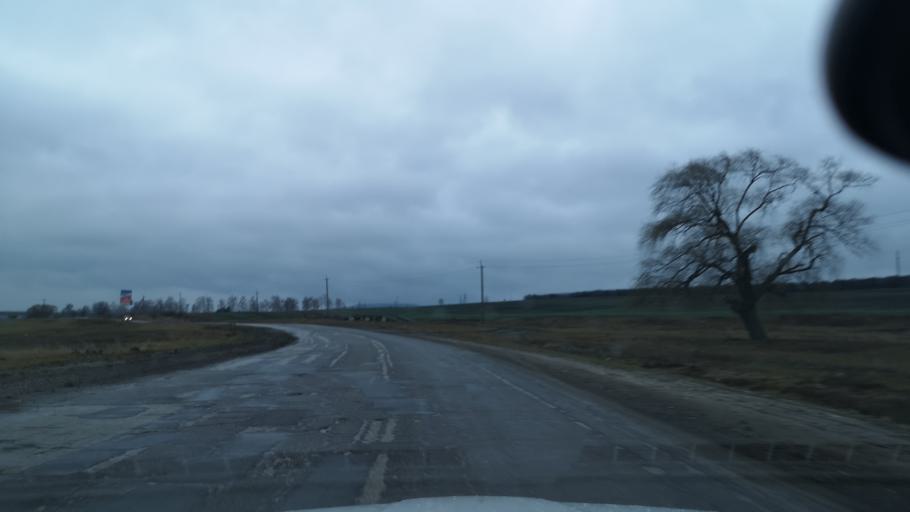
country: MD
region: Singerei
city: Bilicenii Vechi
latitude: 47.5895
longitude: 28.0112
